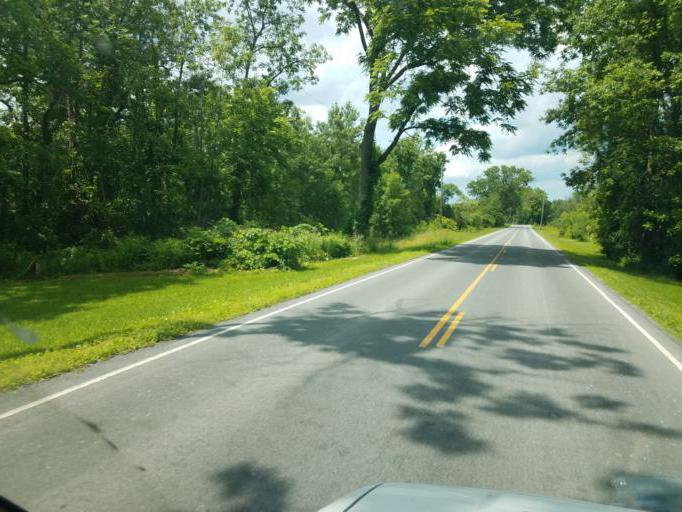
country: US
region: New York
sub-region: Seneca County
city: Waterloo
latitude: 42.9910
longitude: -76.8698
